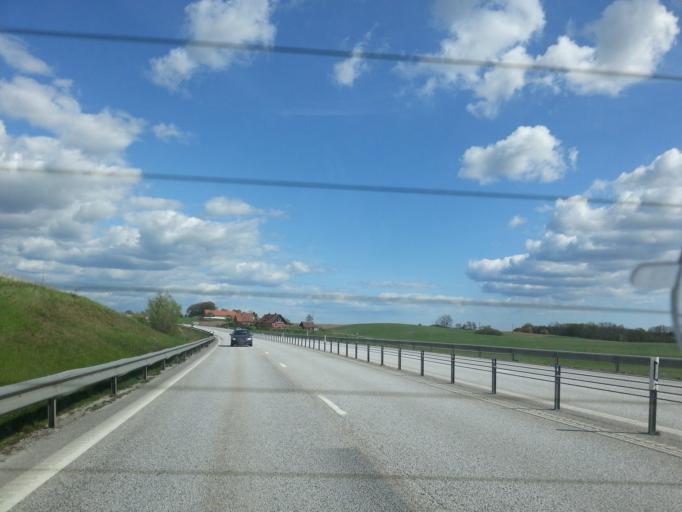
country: SE
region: Skane
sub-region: Skurups Kommun
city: Skurup
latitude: 55.4924
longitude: 13.4592
